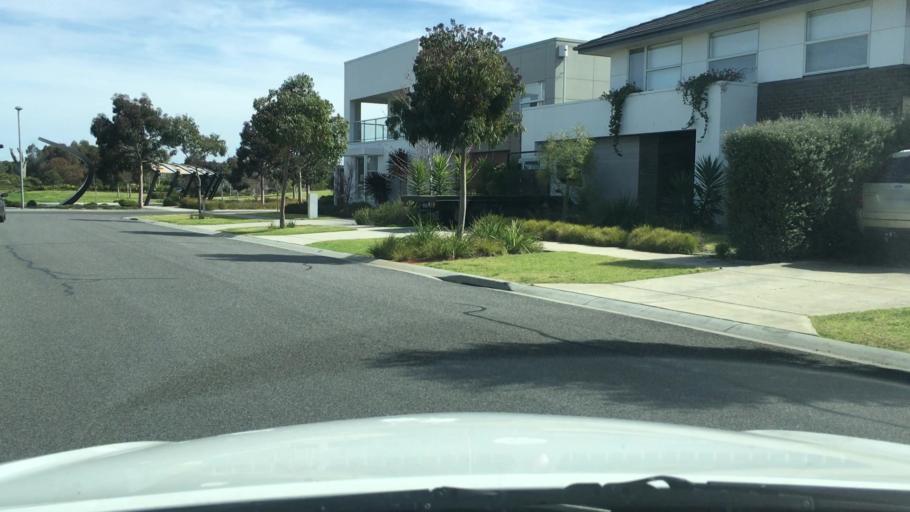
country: AU
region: Victoria
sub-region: Kingston
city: Waterways
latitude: -38.0122
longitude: 145.1386
